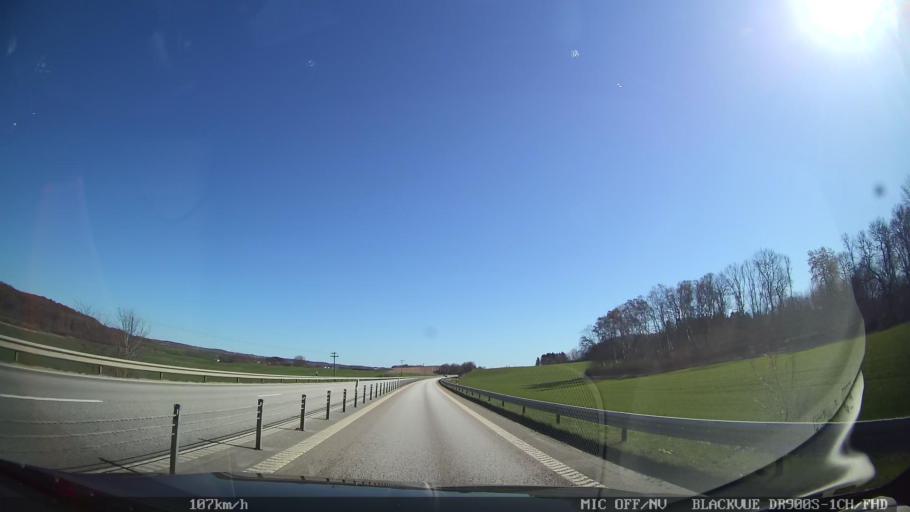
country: SE
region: Skane
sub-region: Skurups Kommun
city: Skurup
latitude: 55.4940
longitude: 13.4922
